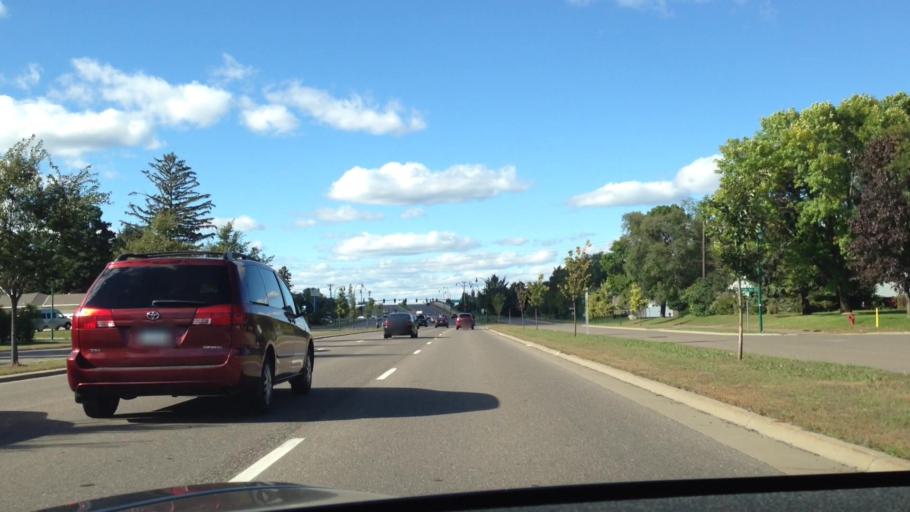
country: US
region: Minnesota
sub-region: Hennepin County
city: Robbinsdale
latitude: 45.0433
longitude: -93.3476
